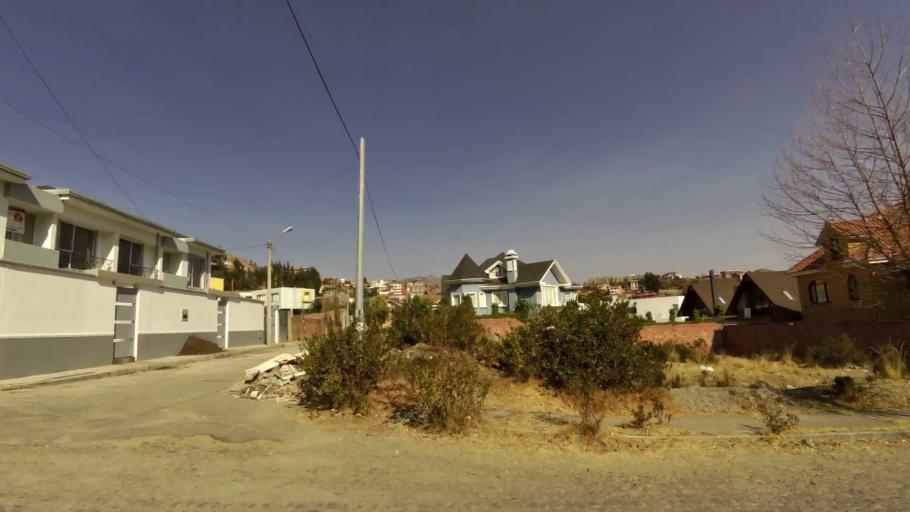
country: BO
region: La Paz
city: La Paz
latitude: -16.5112
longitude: -68.0580
